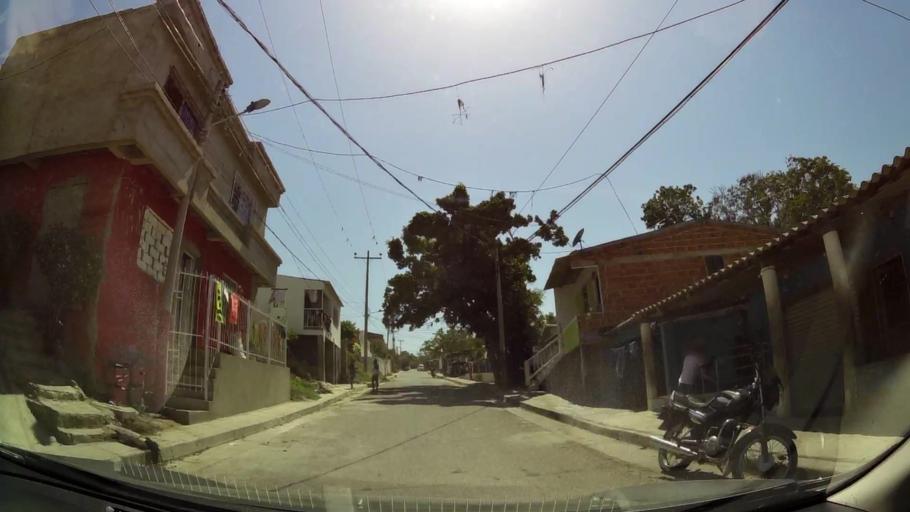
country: CO
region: Bolivar
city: Cartagena
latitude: 10.4299
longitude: -75.5257
